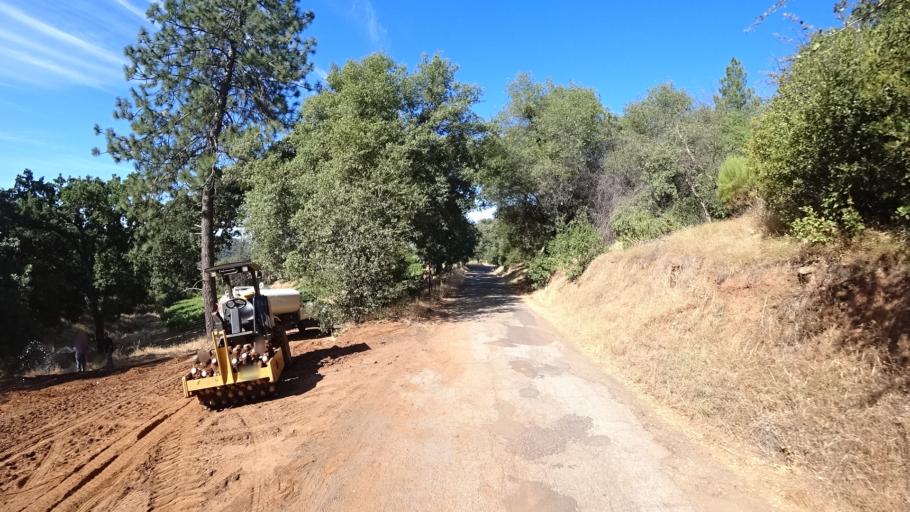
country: US
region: California
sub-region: Calaveras County
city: Mountain Ranch
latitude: 38.1743
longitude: -120.5309
